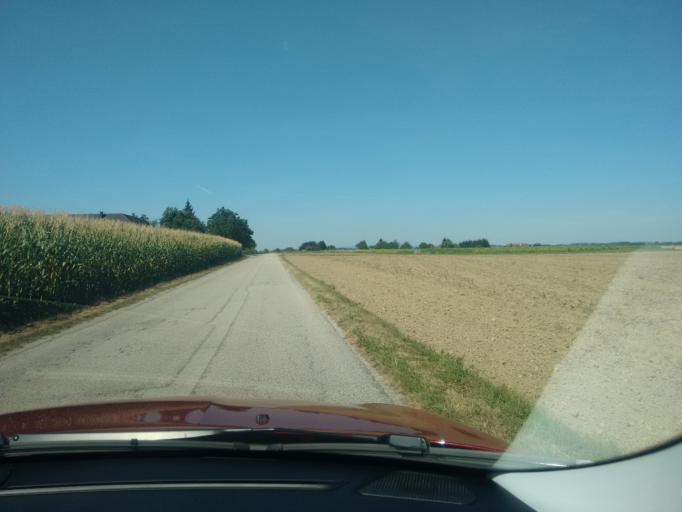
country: AT
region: Upper Austria
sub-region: Wels-Land
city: Steinhaus
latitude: 48.1022
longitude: 14.0358
